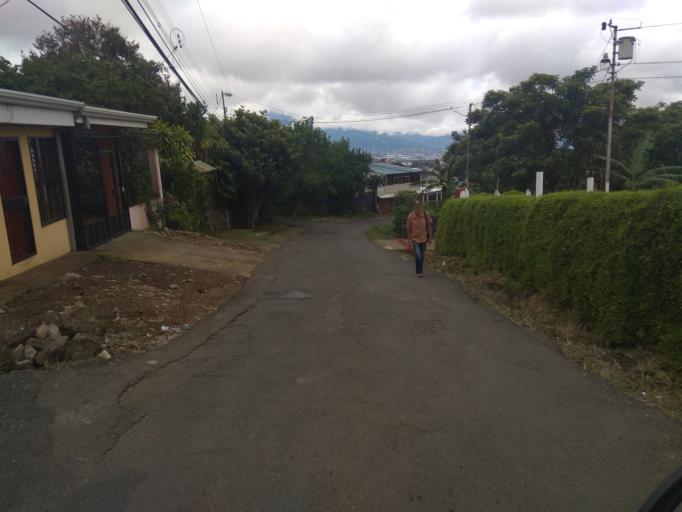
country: CR
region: Heredia
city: San Josecito
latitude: 10.0246
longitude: -84.1033
